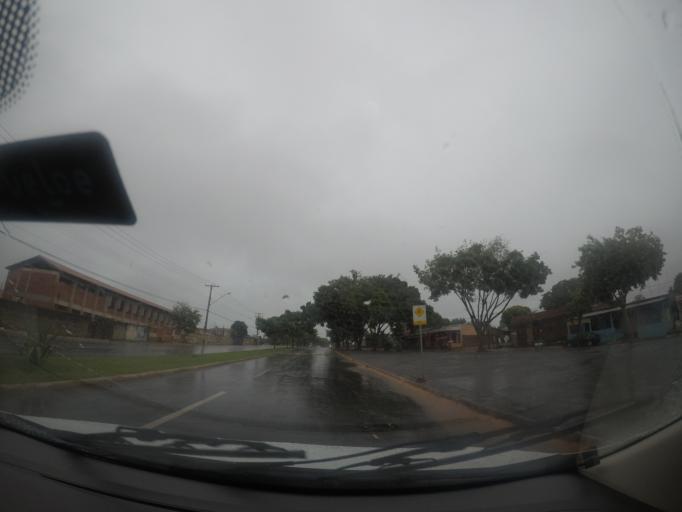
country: BR
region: Goias
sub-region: Goiania
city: Goiania
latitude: -16.6046
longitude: -49.3350
